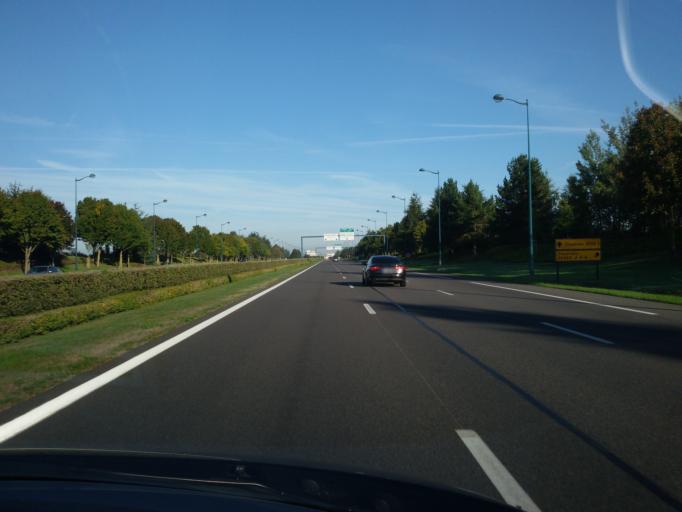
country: FR
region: Ile-de-France
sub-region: Departement de Seine-et-Marne
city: Bailly-Romainvilliers
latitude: 48.8491
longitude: 2.8076
